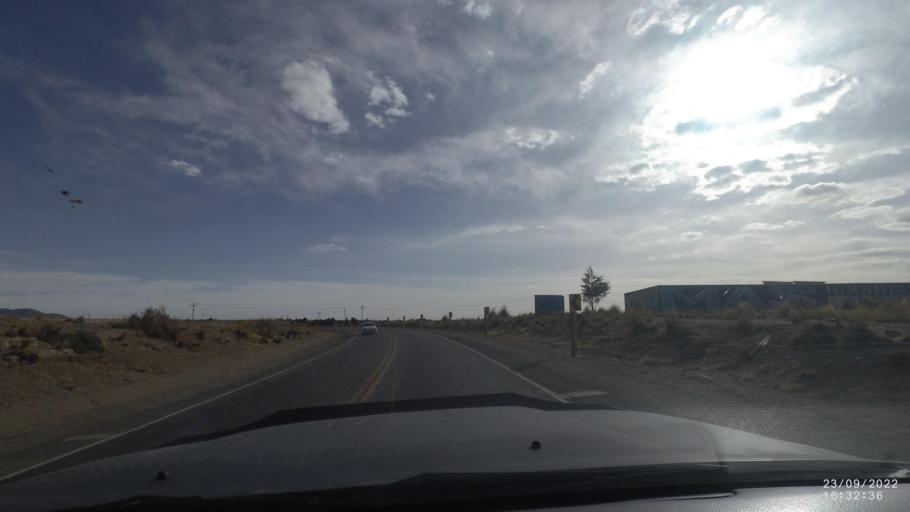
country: BO
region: Oruro
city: Machacamarca
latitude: -18.1639
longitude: -67.0082
